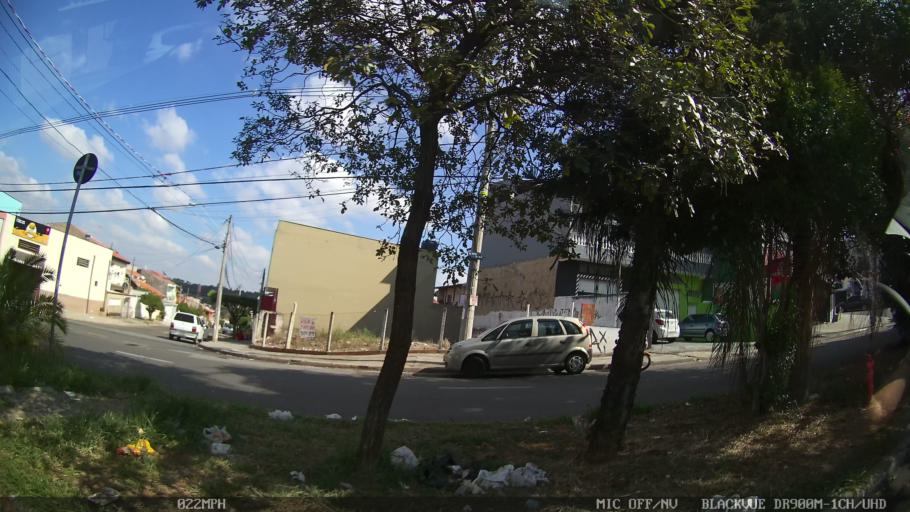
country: BR
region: Sao Paulo
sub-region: Campinas
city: Campinas
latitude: -22.9392
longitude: -47.1199
